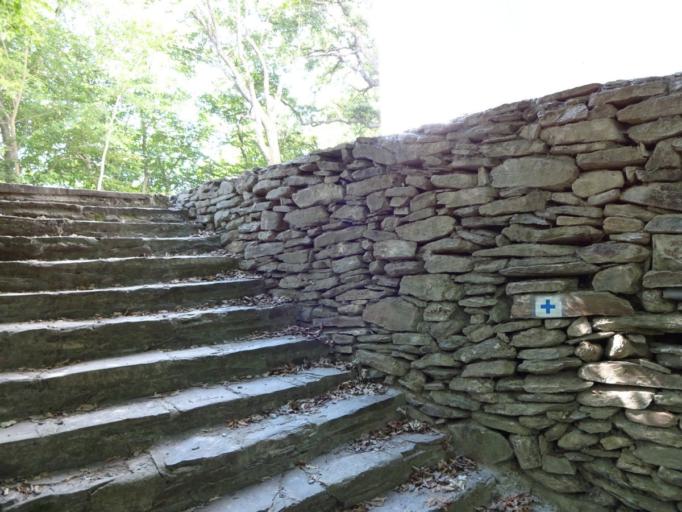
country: AT
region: Burgenland
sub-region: Politischer Bezirk Oberwart
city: Rechnitz
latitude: 47.3508
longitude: 16.4789
